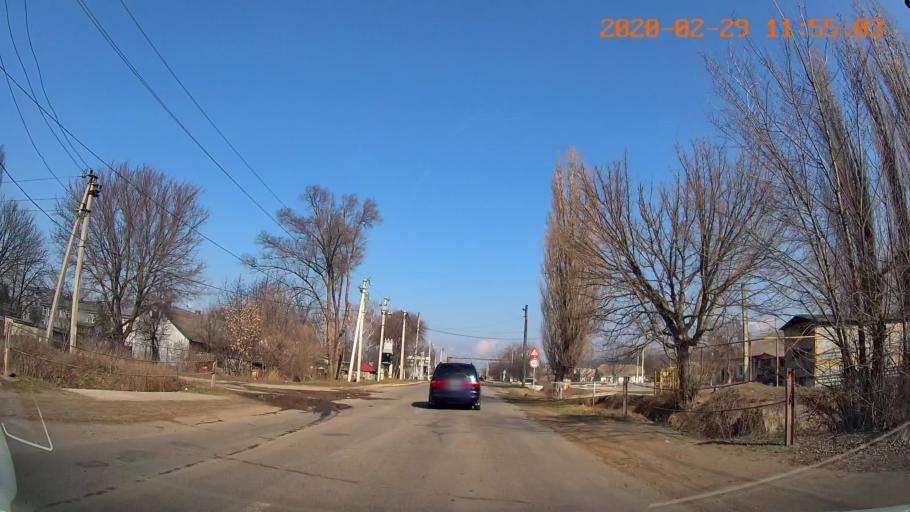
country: MD
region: Telenesti
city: Ribnita
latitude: 47.7878
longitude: 28.9969
